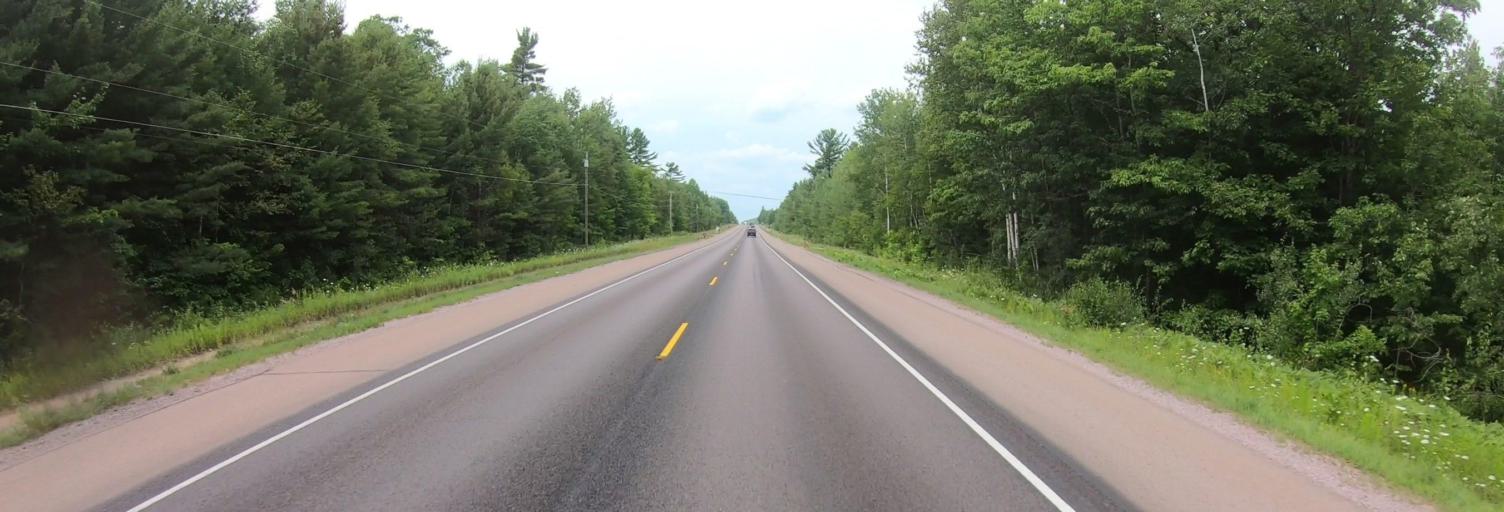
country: US
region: Michigan
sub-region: Marquette County
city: Trowbridge Park
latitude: 46.4713
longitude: -87.4429
